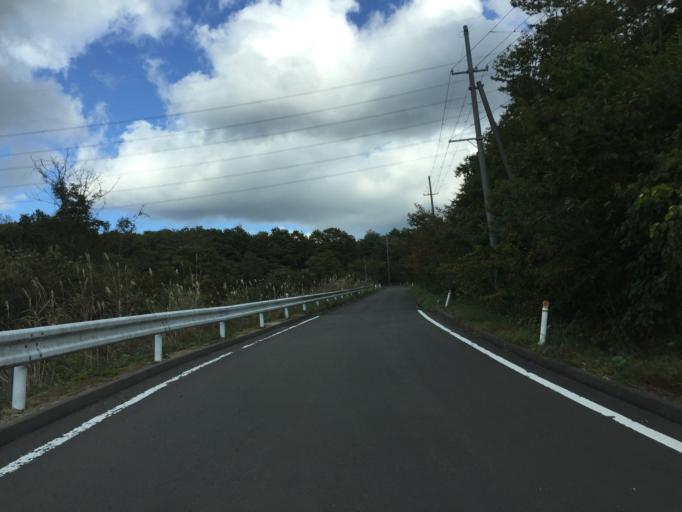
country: JP
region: Miyagi
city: Marumori
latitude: 37.8199
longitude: 140.7519
